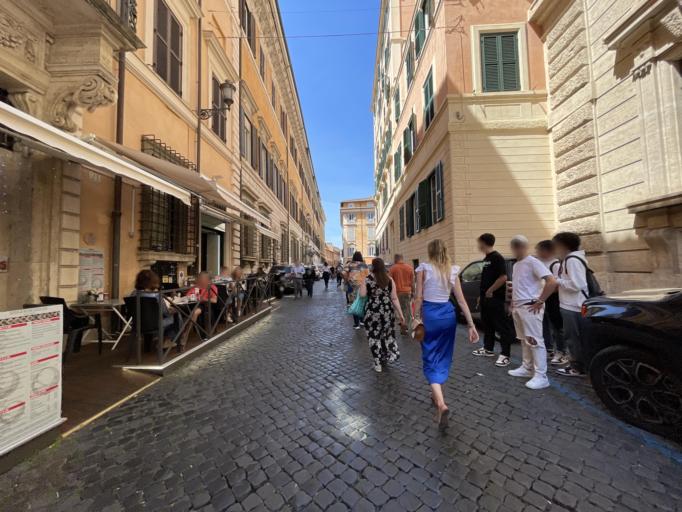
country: IT
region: Latium
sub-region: Citta metropolitana di Roma Capitale
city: Rome
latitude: 41.8992
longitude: 12.4843
